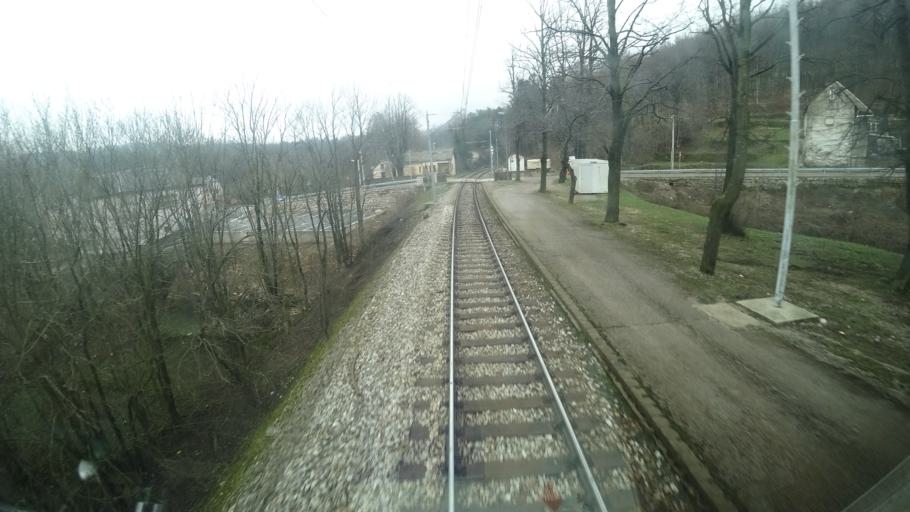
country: HR
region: Primorsko-Goranska
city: Hreljin
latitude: 45.2883
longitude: 14.6509
